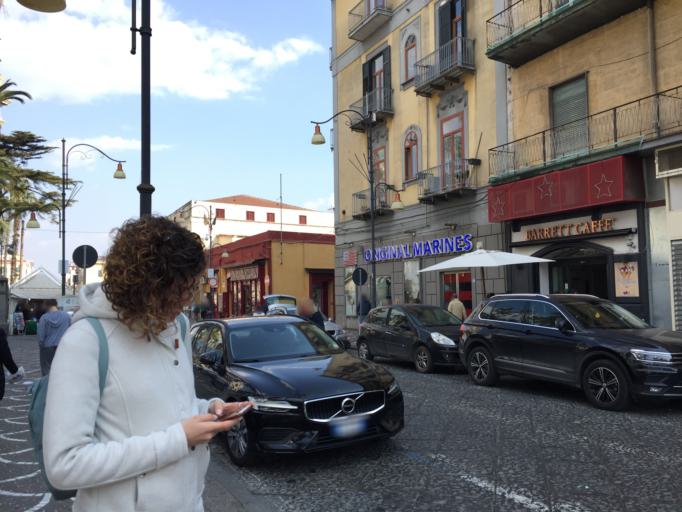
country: IT
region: Campania
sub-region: Provincia di Napoli
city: Pompei
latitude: 40.7495
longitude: 14.4988
